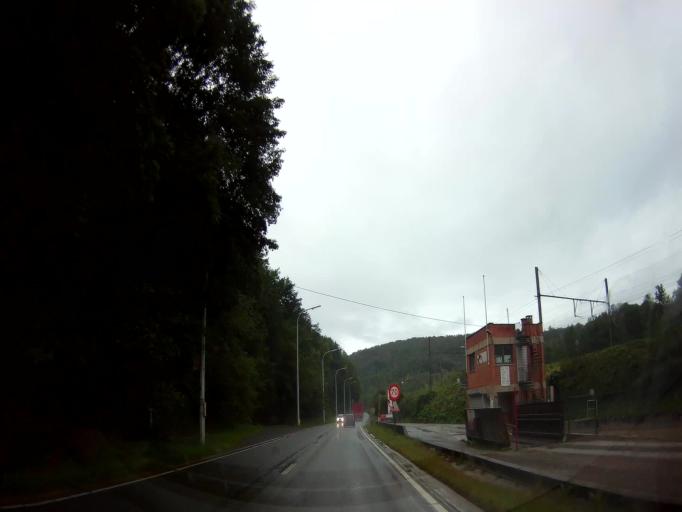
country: BE
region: Wallonia
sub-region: Province de Liege
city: Trooz
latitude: 50.5669
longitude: 5.7010
